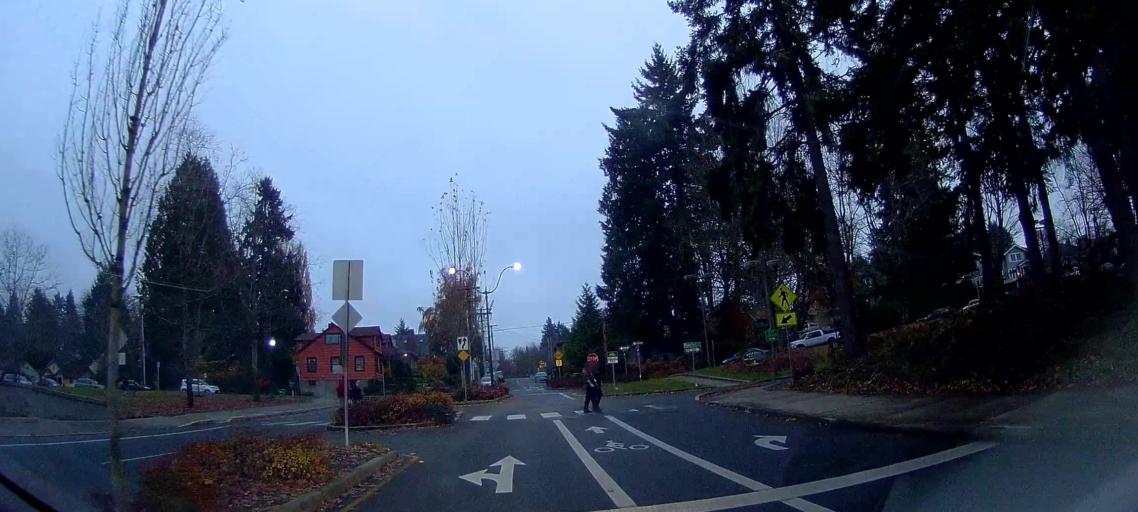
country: US
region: Washington
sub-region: Thurston County
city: Olympia
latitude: 47.0342
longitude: -122.8959
